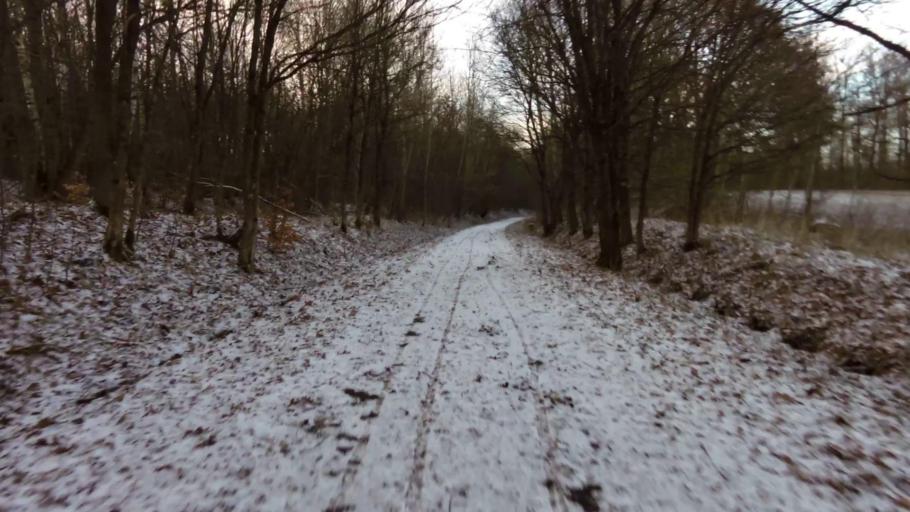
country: PL
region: West Pomeranian Voivodeship
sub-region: Powiat swidwinski
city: Polczyn-Zdroj
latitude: 53.6595
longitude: 16.0307
